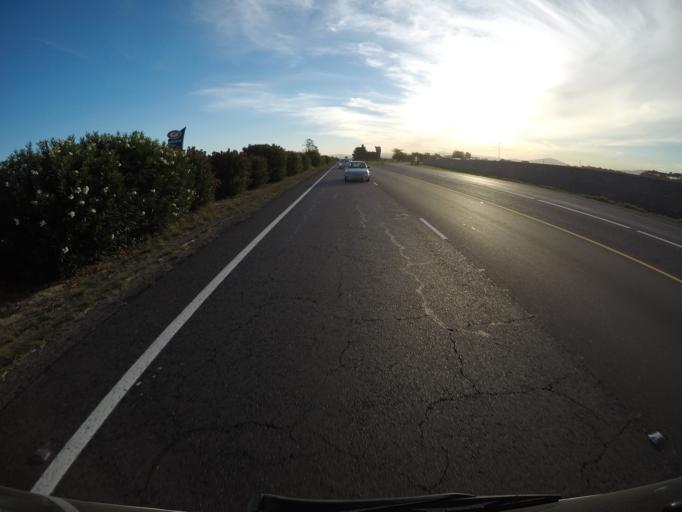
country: ZA
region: Western Cape
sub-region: City of Cape Town
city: Kraaifontein
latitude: -33.8267
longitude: 18.7668
